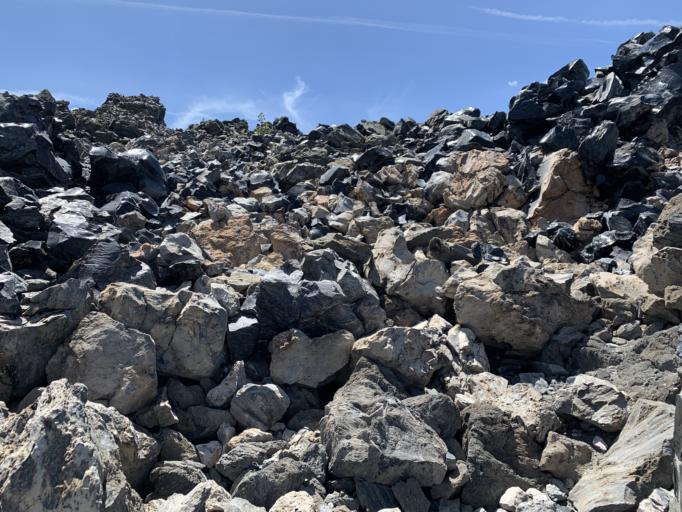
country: US
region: Oregon
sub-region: Deschutes County
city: Three Rivers
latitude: 43.7033
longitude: -121.2357
